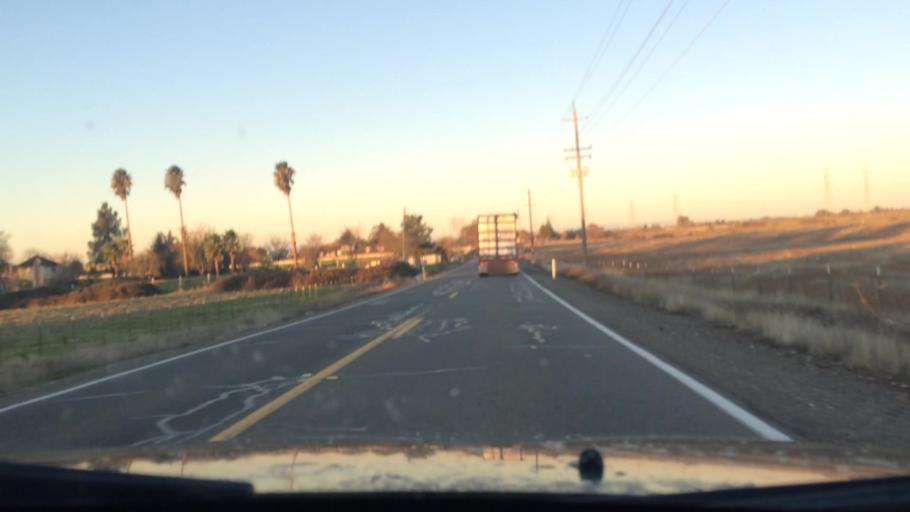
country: US
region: California
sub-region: Sacramento County
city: Vineyard
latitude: 38.5109
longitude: -121.3014
